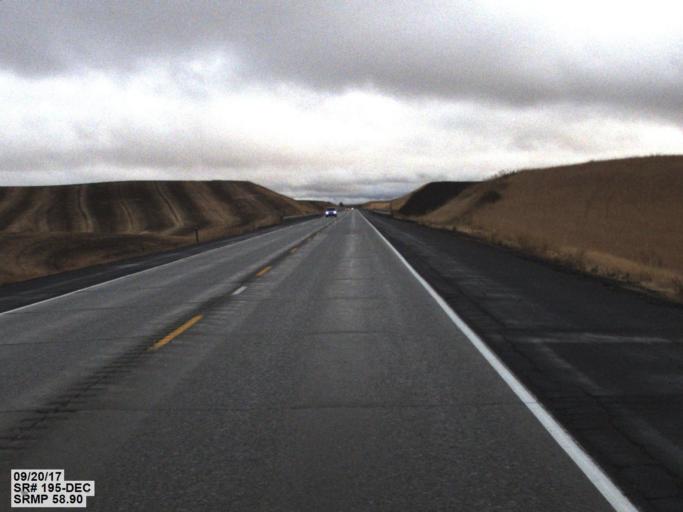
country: US
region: Washington
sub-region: Whitman County
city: Colfax
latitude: 47.1589
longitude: -117.3786
